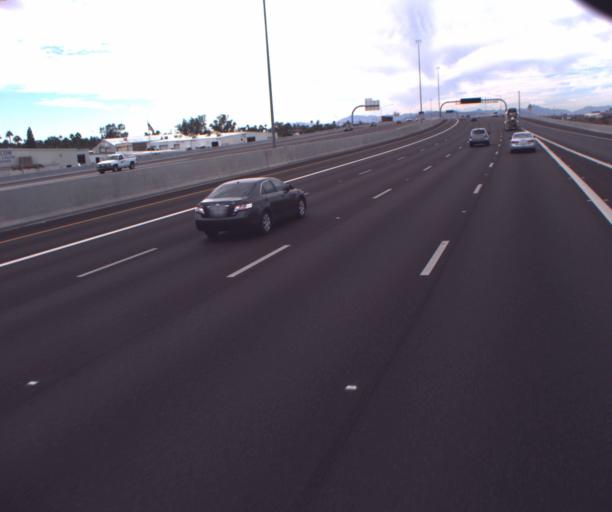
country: US
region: Arizona
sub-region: Maricopa County
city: Mesa
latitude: 33.4540
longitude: -111.8438
